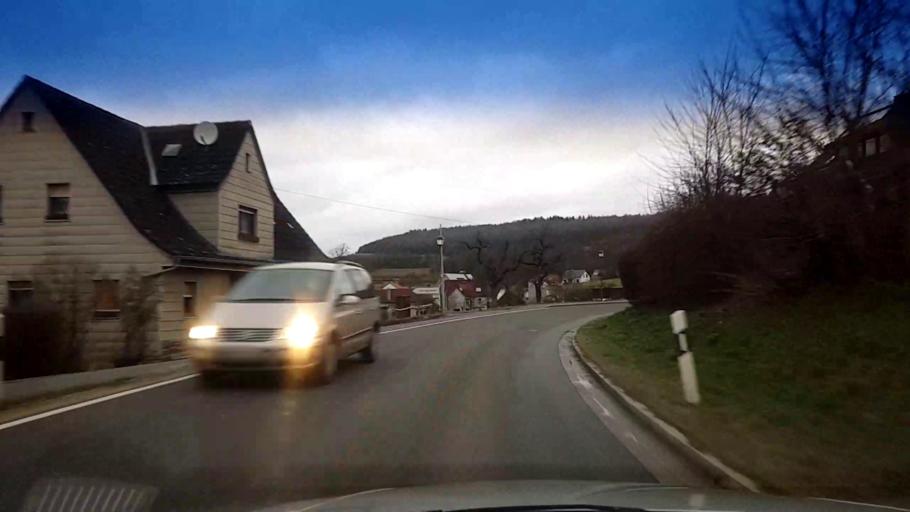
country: DE
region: Bavaria
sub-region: Upper Franconia
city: Wattendorf
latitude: 50.0599
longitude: 11.0742
